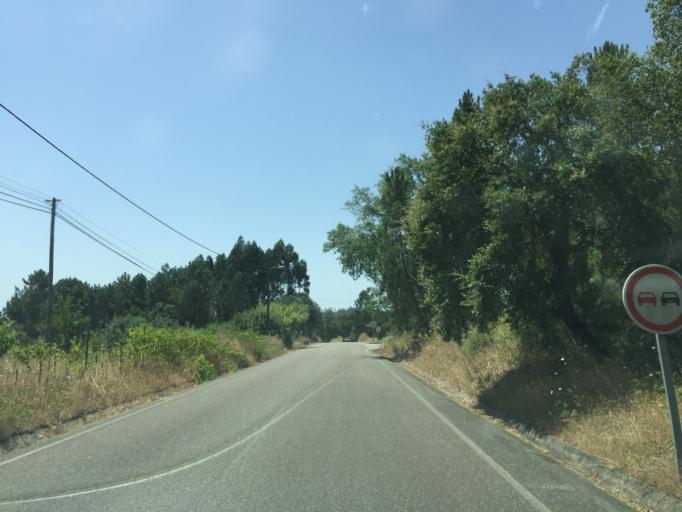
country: PT
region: Santarem
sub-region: Ferreira do Zezere
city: Ferreira do Zezere
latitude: 39.6247
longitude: -8.3101
